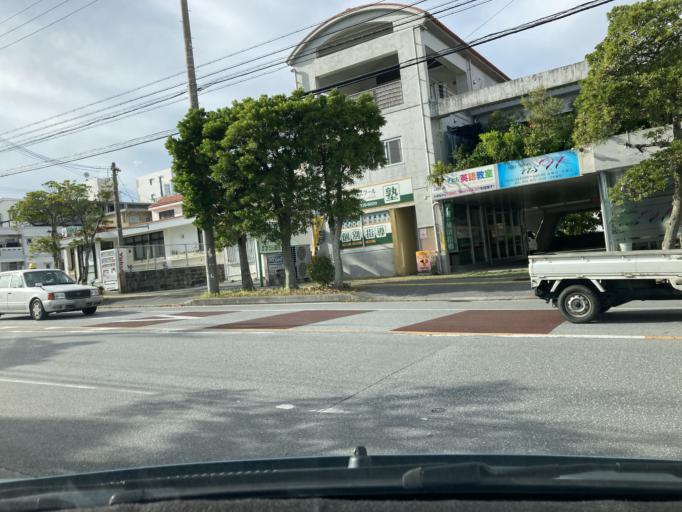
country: JP
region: Okinawa
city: Okinawa
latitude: 26.3428
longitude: 127.8248
